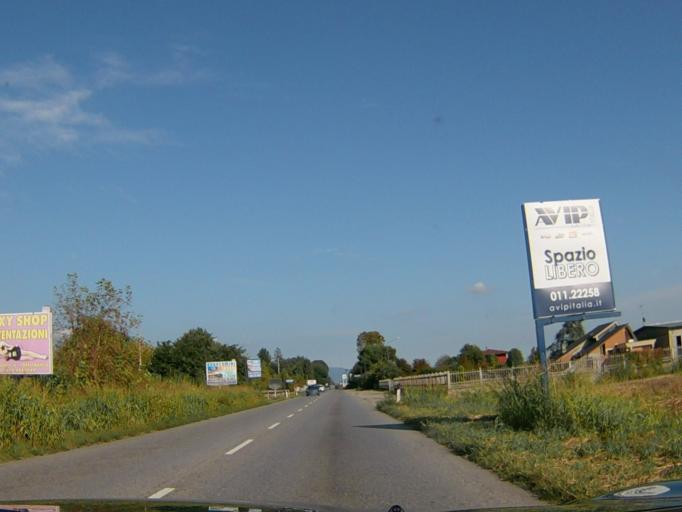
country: IT
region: Lombardy
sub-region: Provincia di Brescia
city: Lodetto
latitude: 45.5595
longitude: 10.0221
